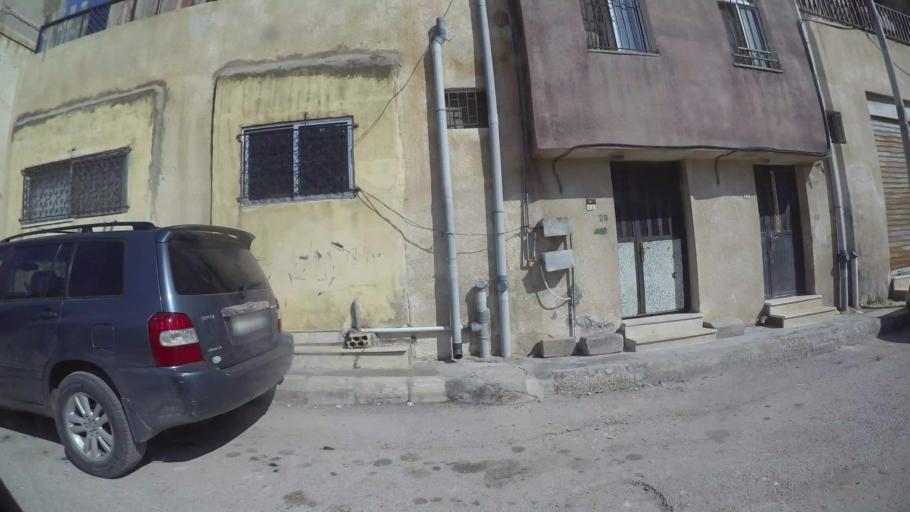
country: JO
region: Amman
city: Al Jubayhah
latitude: 32.0773
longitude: 35.8454
